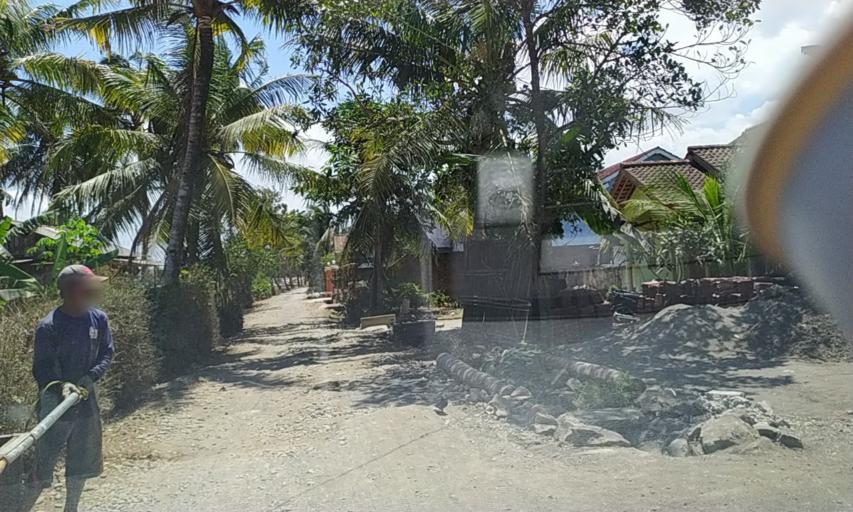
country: ID
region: Central Java
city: Mernek
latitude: -7.6262
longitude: 109.1756
